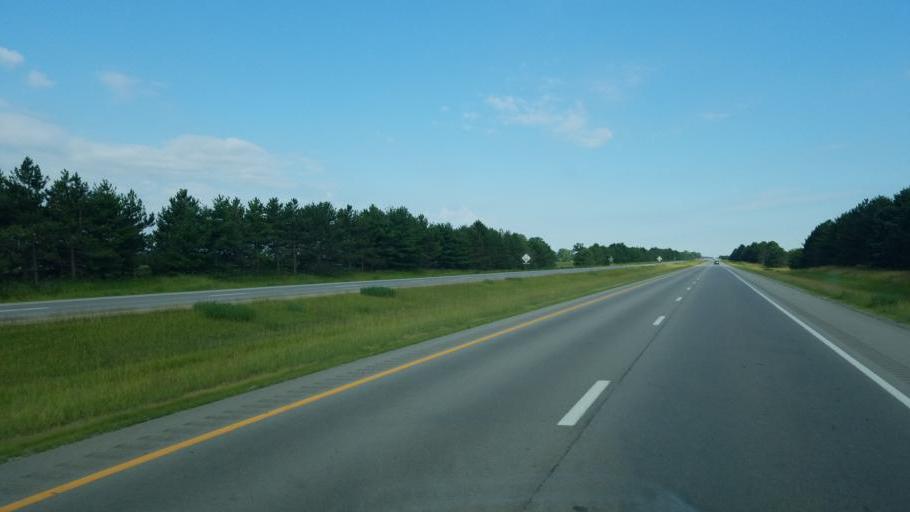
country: US
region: Ohio
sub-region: Wyandot County
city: Carey
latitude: 40.9524
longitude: -83.4305
